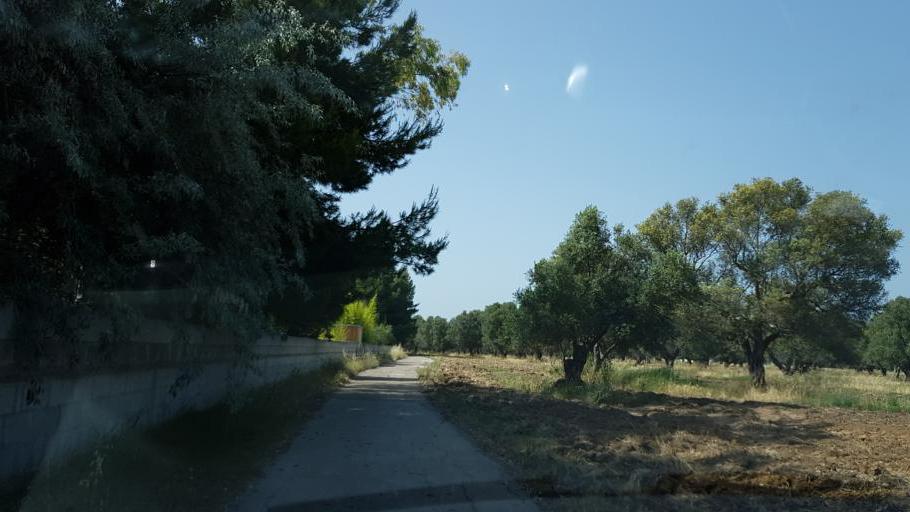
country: IT
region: Apulia
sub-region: Provincia di Brindisi
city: Brindisi
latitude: 40.6584
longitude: 17.9282
